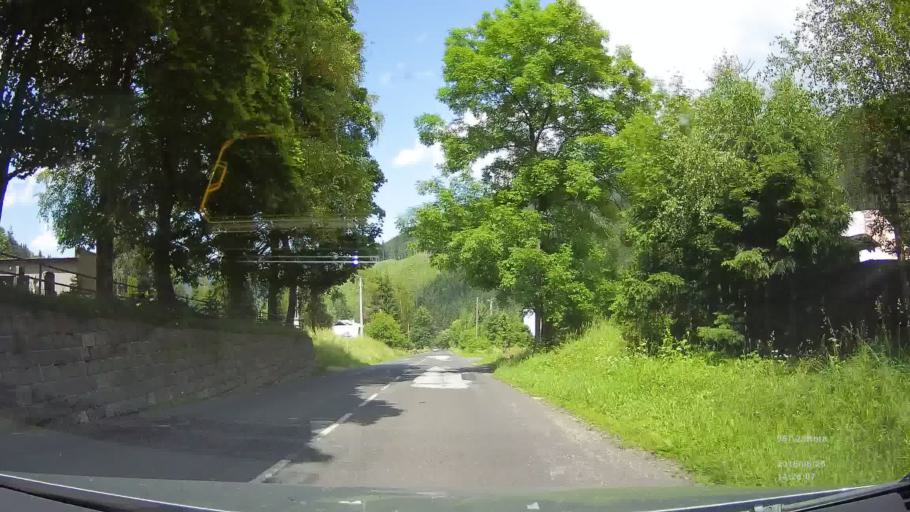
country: SK
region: Zilinsky
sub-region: Okres Zilina
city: Liptovsky Hradok
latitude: 48.9501
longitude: 19.7698
